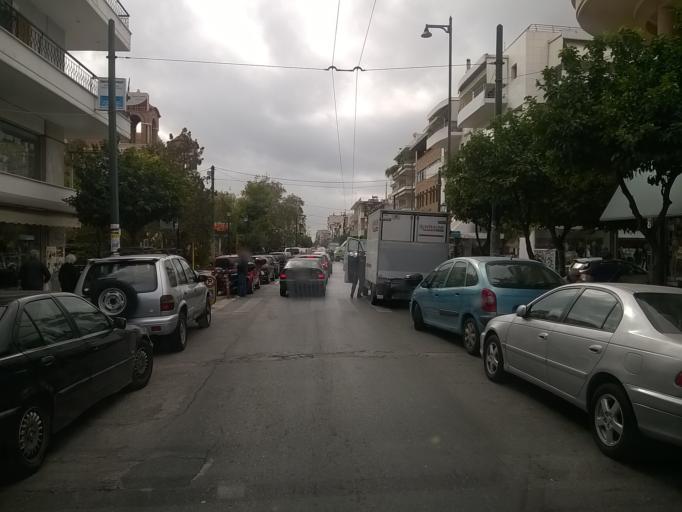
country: GR
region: Attica
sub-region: Nomarchia Athinas
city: Moskhaton
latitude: 37.9528
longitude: 23.6793
